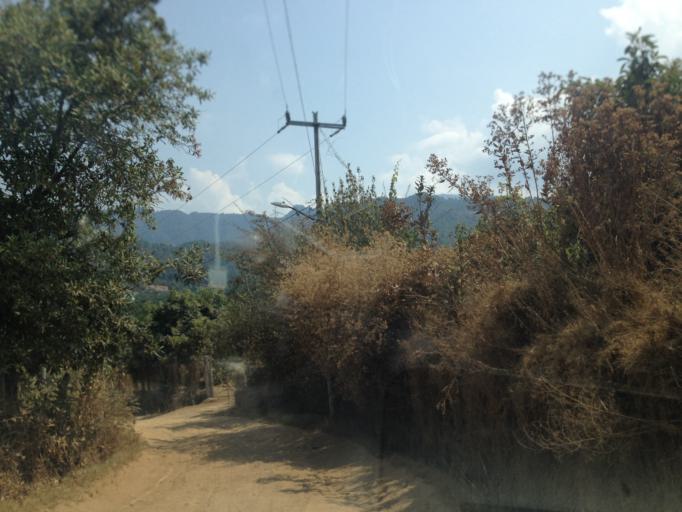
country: MX
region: Michoacan
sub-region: Zitacuaro
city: Macutzio
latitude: 19.4916
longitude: -100.3300
